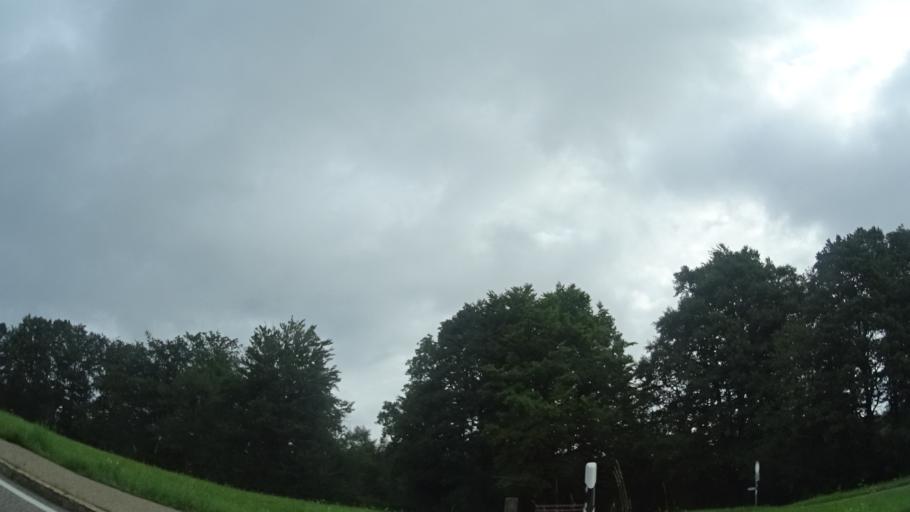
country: DE
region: Baden-Wuerttemberg
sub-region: Karlsruhe Region
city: Dobel
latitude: 48.8193
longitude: 8.4748
